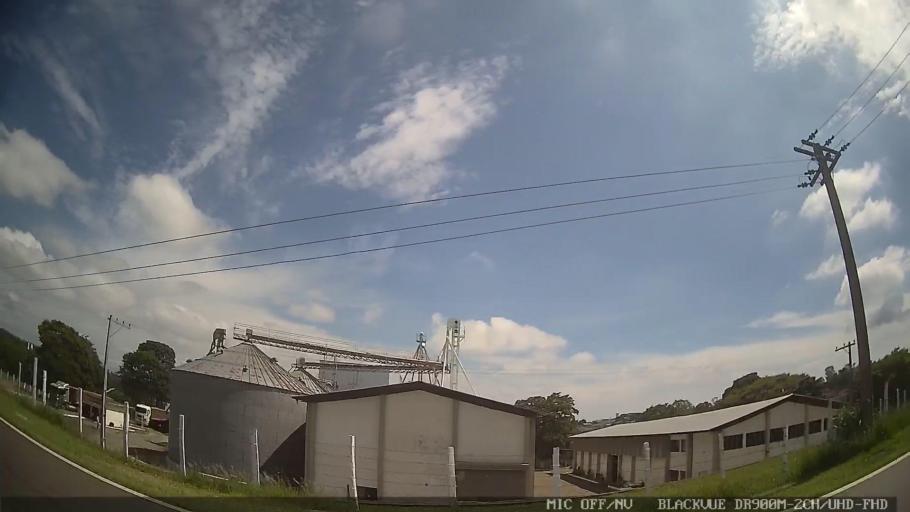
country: BR
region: Sao Paulo
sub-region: Tiete
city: Tiete
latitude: -23.1182
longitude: -47.7166
